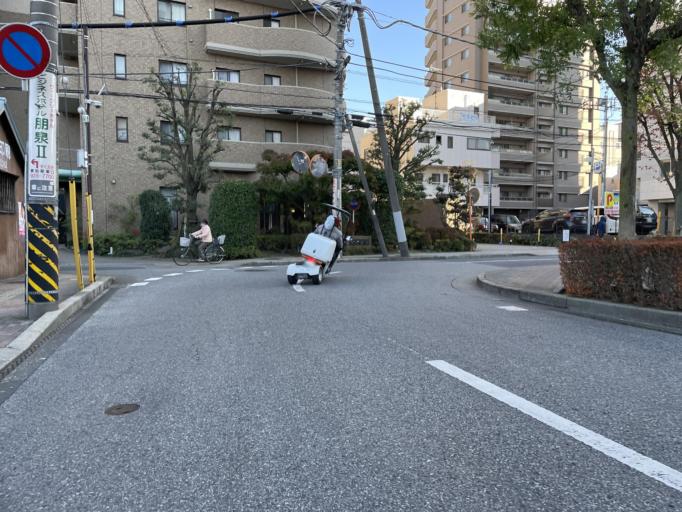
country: JP
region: Saitama
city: Soka
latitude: 35.8291
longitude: 139.8050
